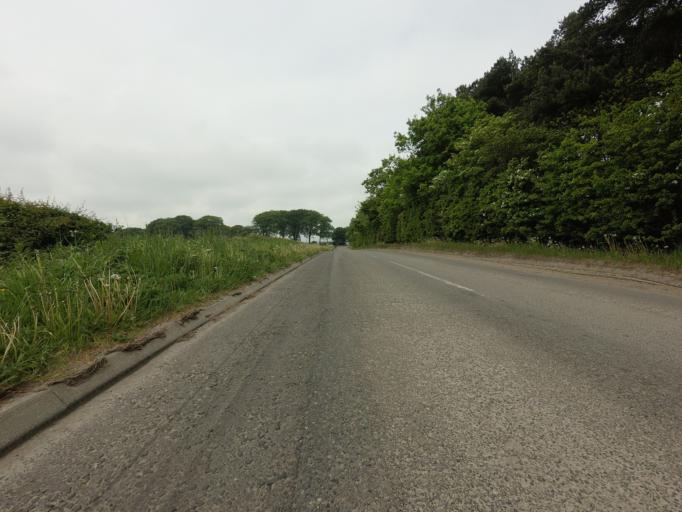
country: GB
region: Scotland
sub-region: Fife
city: Townhill
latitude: 56.0975
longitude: -3.4443
